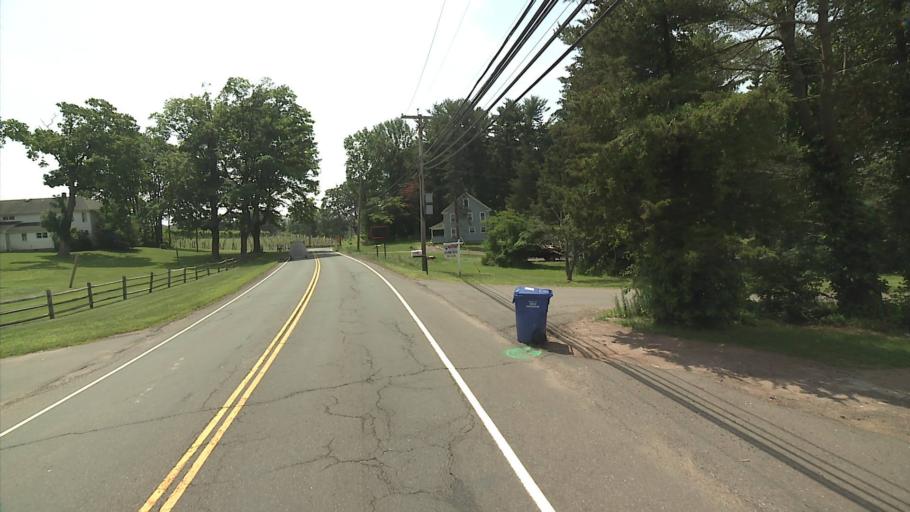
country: US
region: Connecticut
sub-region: New Haven County
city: North Branford
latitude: 41.3079
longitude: -72.7712
